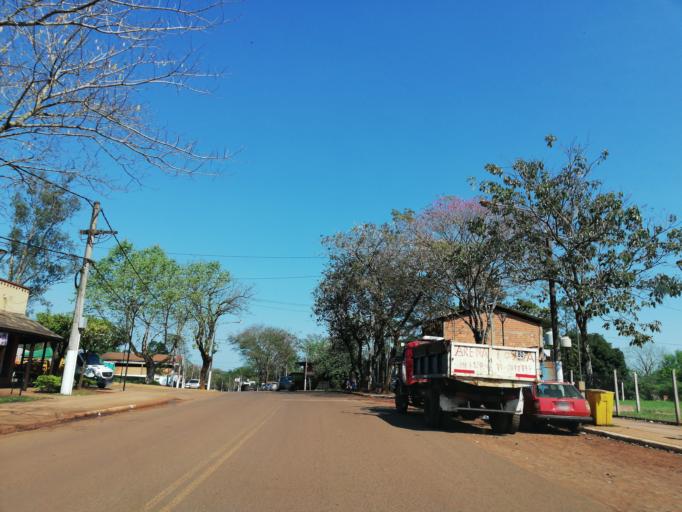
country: AR
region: Misiones
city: Puerto Eldorado
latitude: -26.4071
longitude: -54.6671
